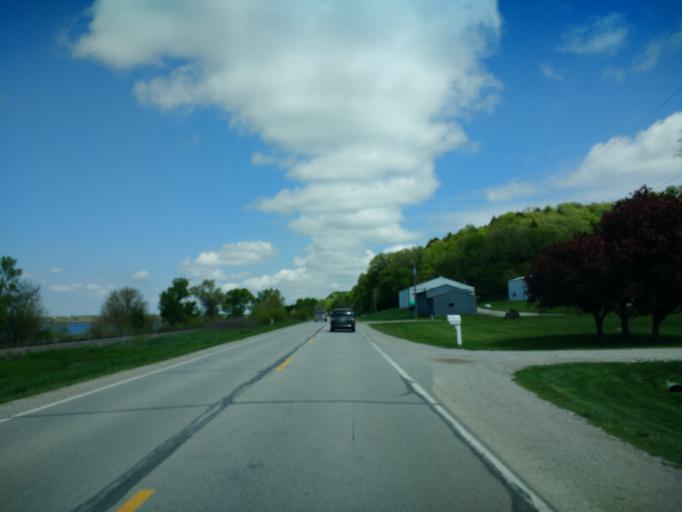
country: US
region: Iowa
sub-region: Harrison County
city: Missouri Valley
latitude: 41.4412
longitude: -95.8701
